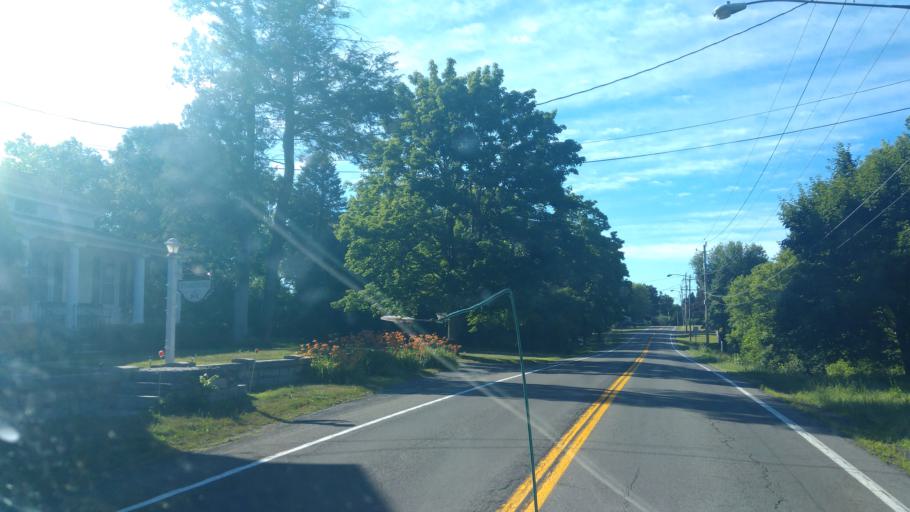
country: US
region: New York
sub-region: Wayne County
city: Lyons
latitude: 43.0222
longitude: -76.9878
